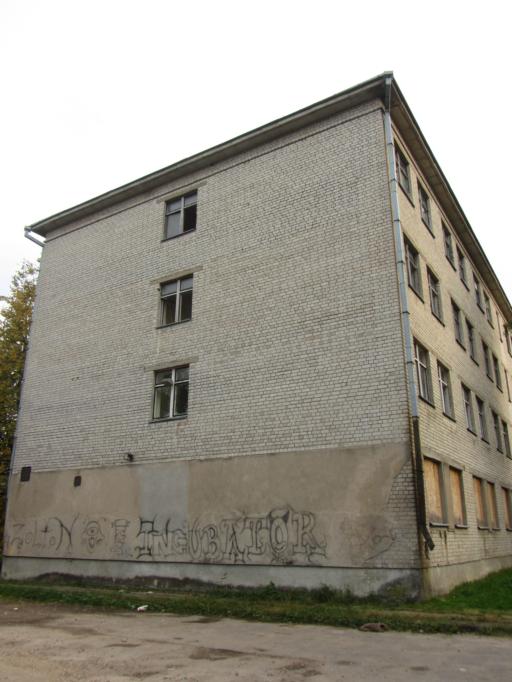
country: LT
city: Trakai
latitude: 54.6390
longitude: 24.9402
